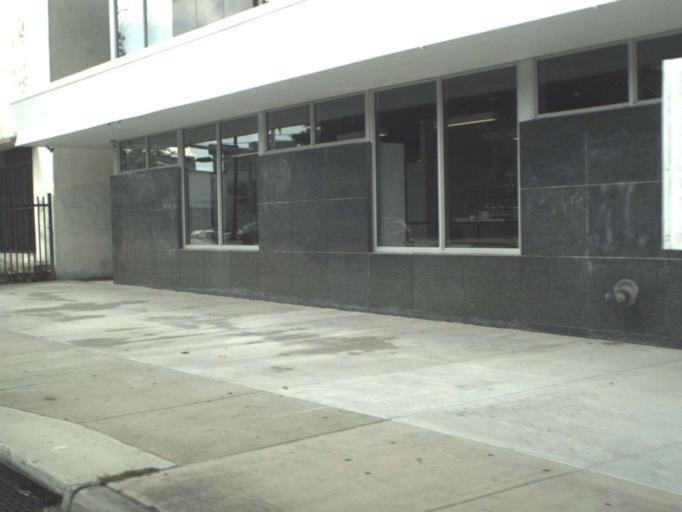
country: US
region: Florida
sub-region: Miami-Dade County
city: El Portal
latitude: 25.8455
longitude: -80.1846
